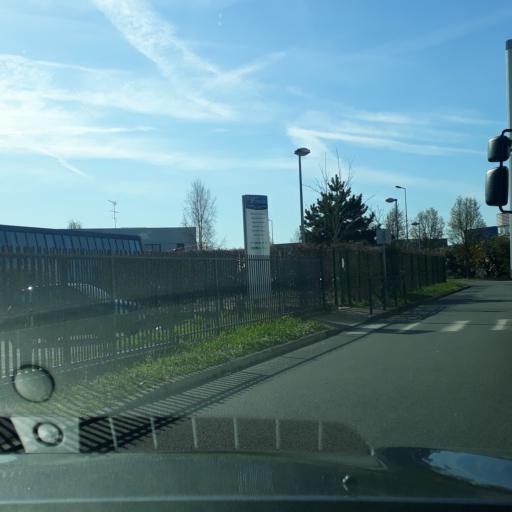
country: FR
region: Ile-de-France
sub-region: Departement de l'Essonne
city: Mennecy
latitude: 48.5653
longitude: 2.4448
